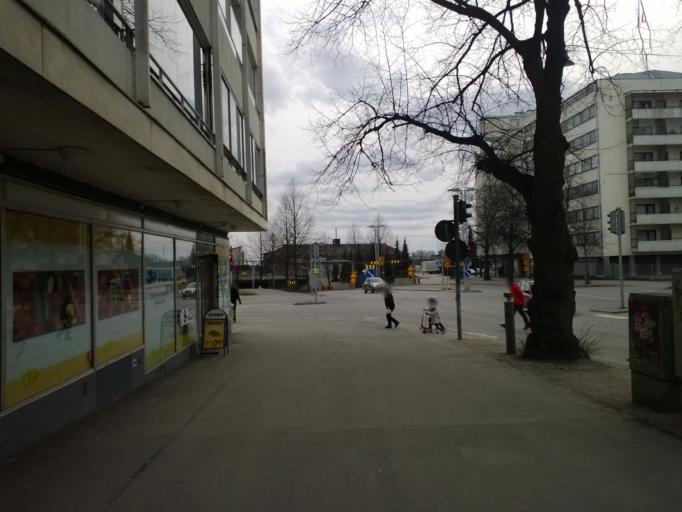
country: FI
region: Paijanne Tavastia
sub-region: Lahti
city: Lahti
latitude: 60.9788
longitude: 25.6596
